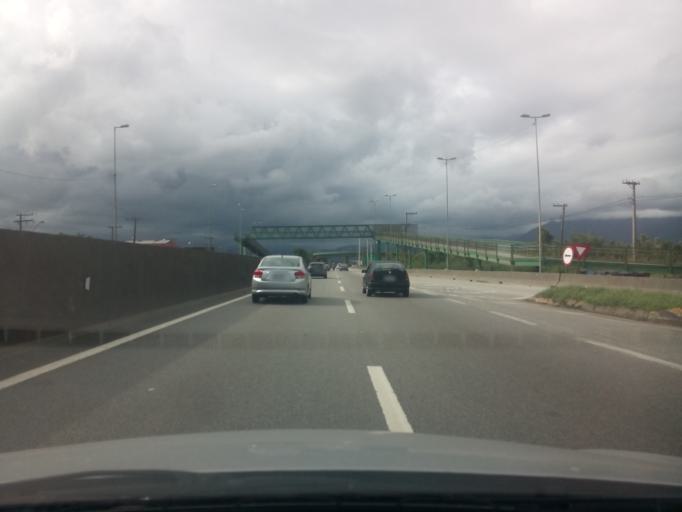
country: BR
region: Sao Paulo
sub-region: Guaruja
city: Guaruja
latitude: -23.9445
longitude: -46.2793
